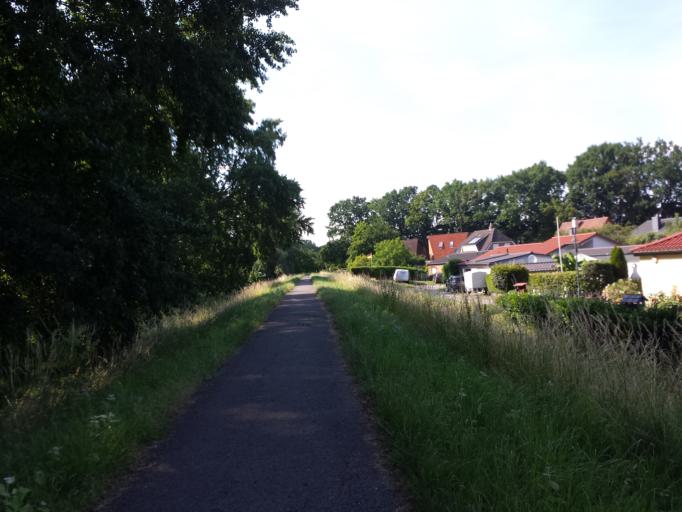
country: DE
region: Lower Saxony
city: Stuhr
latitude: 53.0901
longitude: 8.7470
